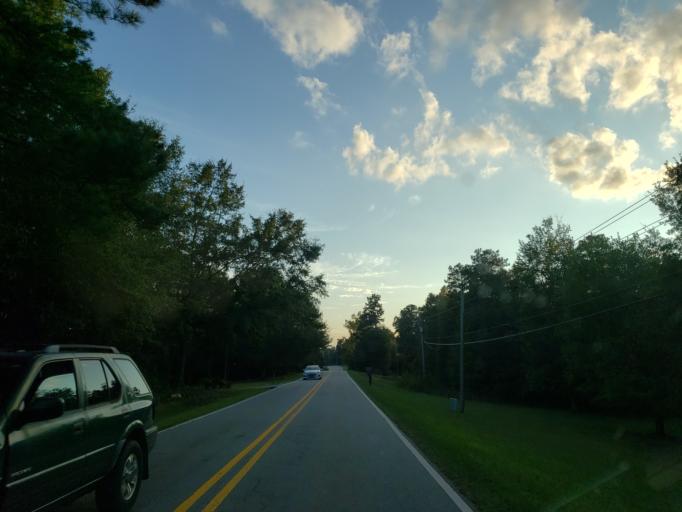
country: US
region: Georgia
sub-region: Carroll County
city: Carrollton
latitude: 33.6096
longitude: -85.0536
